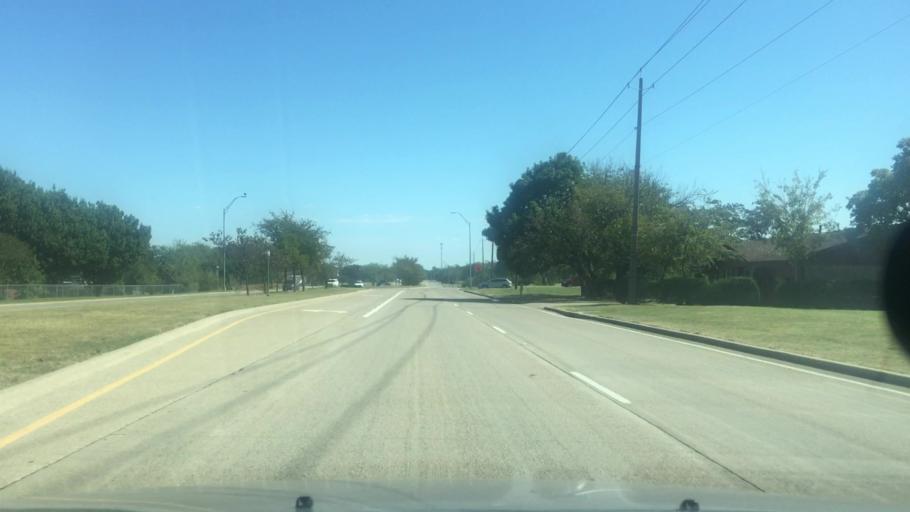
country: US
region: Texas
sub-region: Denton County
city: Denton
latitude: 33.2464
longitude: -97.1445
